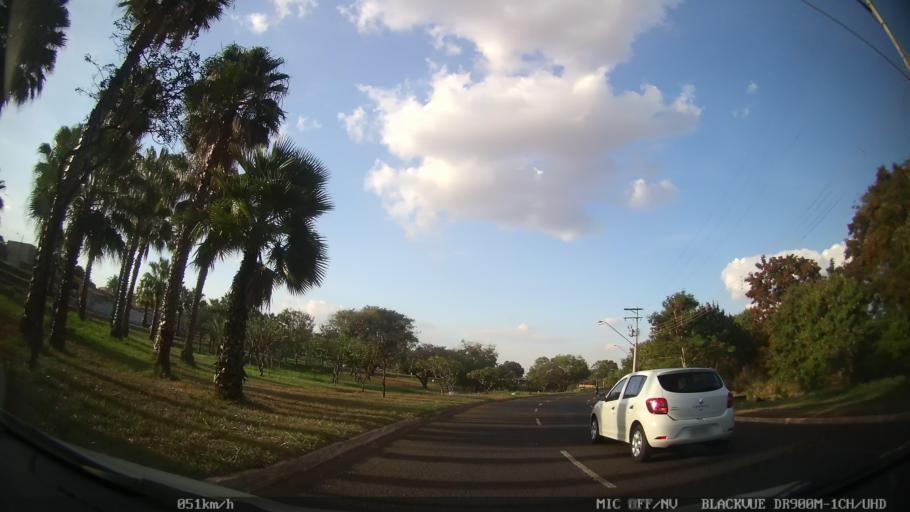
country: BR
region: Sao Paulo
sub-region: Ribeirao Preto
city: Ribeirao Preto
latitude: -21.1621
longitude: -47.8165
